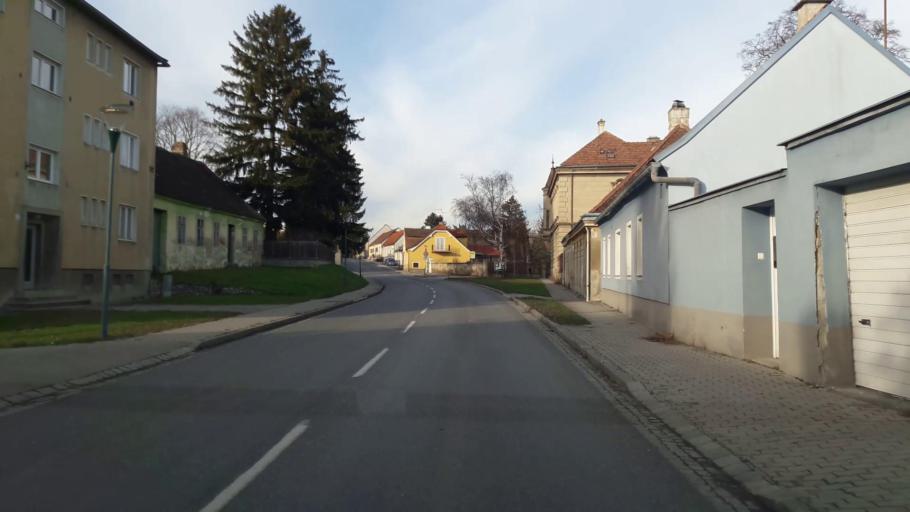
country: AT
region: Lower Austria
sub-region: Politischer Bezirk Ganserndorf
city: Bad Pirawarth
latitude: 48.4561
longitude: 16.5961
